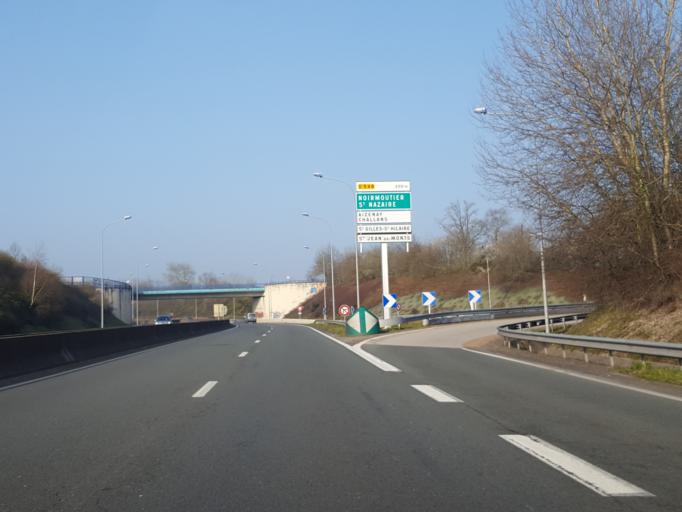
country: FR
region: Pays de la Loire
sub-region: Departement de la Vendee
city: La Roche-sur-Yon
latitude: 46.6882
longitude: -1.4383
